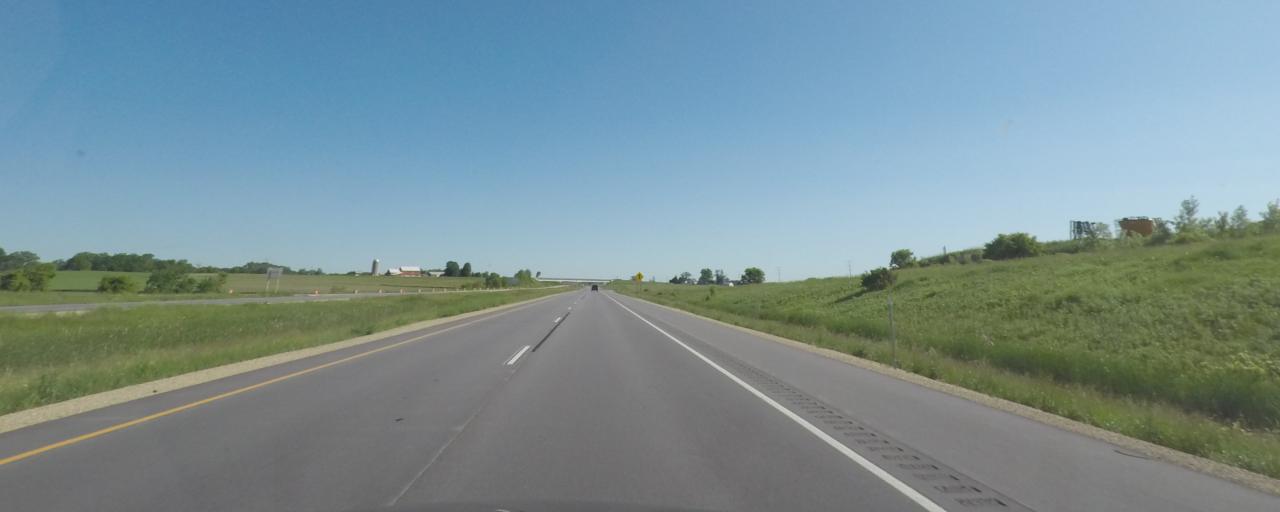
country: US
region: Wisconsin
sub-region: Columbia County
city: Columbus
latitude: 43.3192
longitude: -89.0452
